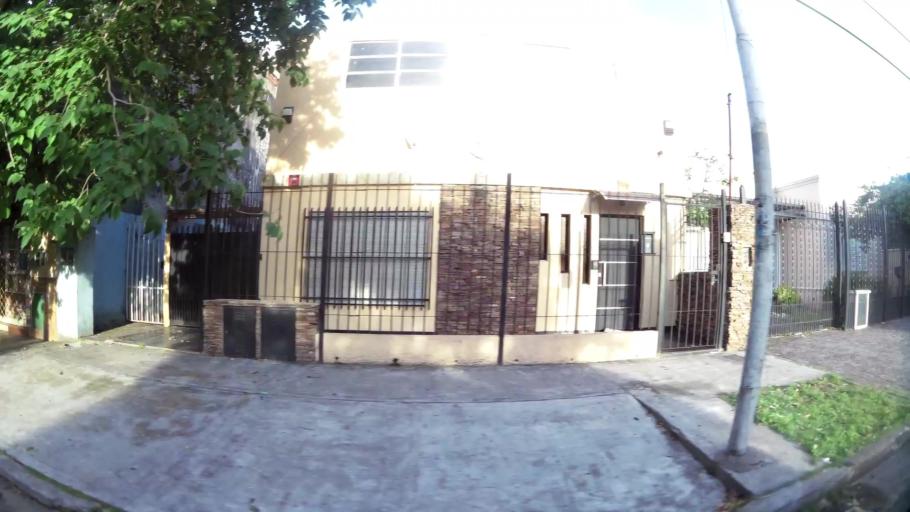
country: AR
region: Buenos Aires
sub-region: Partido de Moron
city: Moron
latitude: -34.6553
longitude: -58.6254
